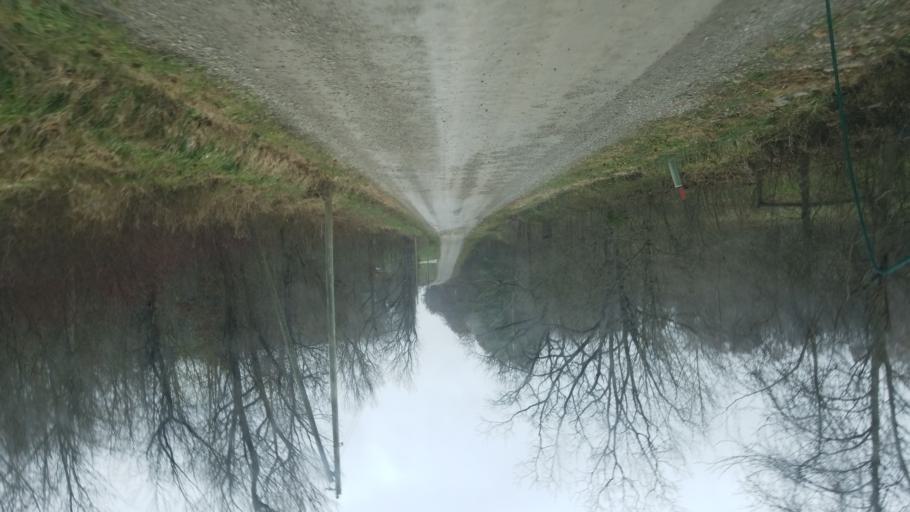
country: US
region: Ohio
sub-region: Huron County
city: New London
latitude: 40.9754
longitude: -82.3815
